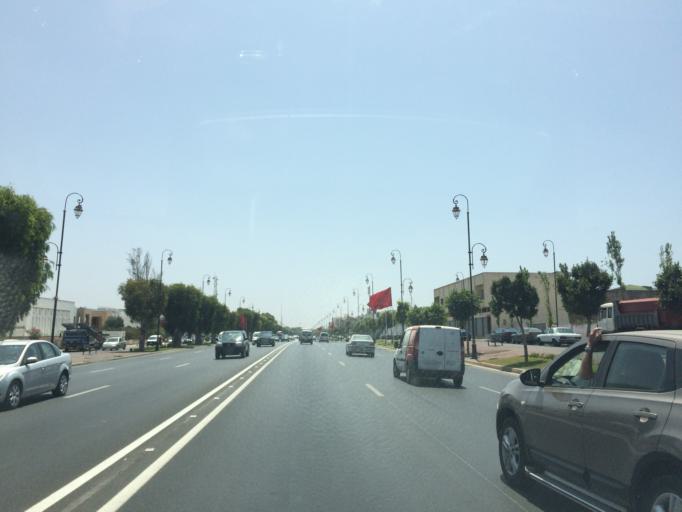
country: MA
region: Rabat-Sale-Zemmour-Zaer
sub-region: Rabat
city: Rabat
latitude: 33.9857
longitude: -6.8702
